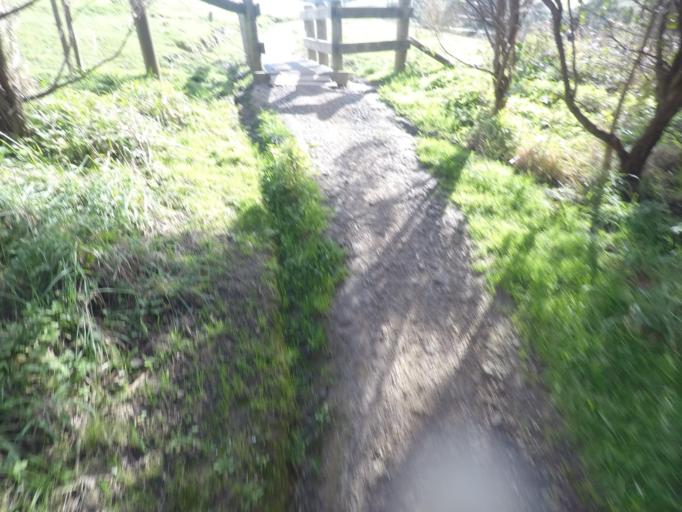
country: NZ
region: Auckland
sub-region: Auckland
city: Manukau City
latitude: -36.9972
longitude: 174.9099
